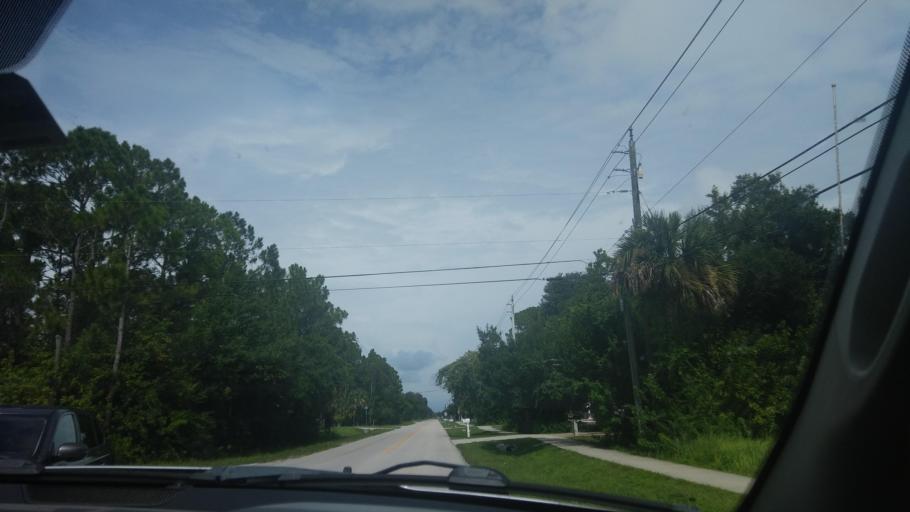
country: US
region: Florida
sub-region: Indian River County
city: Fellsmere
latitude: 27.7526
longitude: -80.5214
